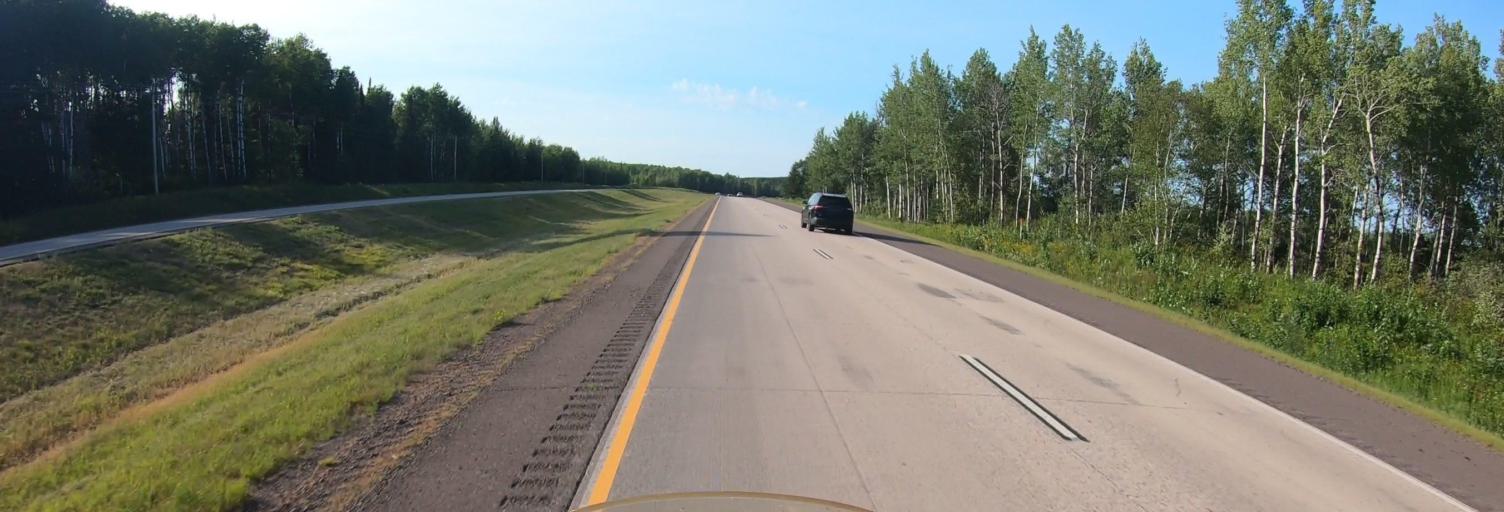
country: US
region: Minnesota
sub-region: Carlton County
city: Cloquet
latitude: 46.9738
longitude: -92.4680
